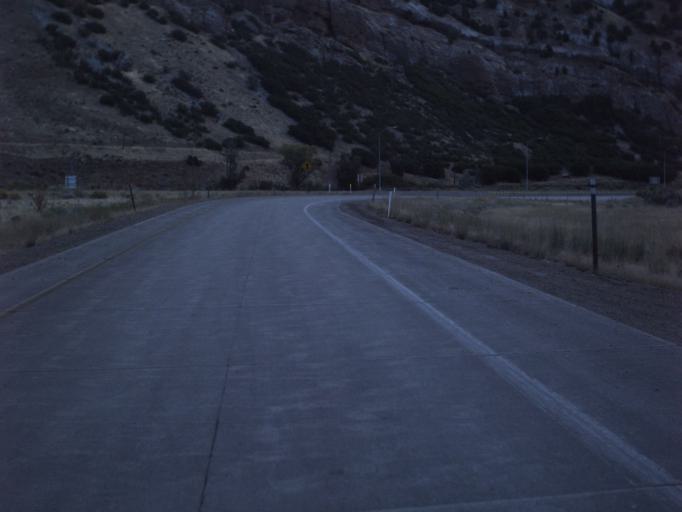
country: US
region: Utah
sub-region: Morgan County
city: Morgan
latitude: 41.0570
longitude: -111.5380
